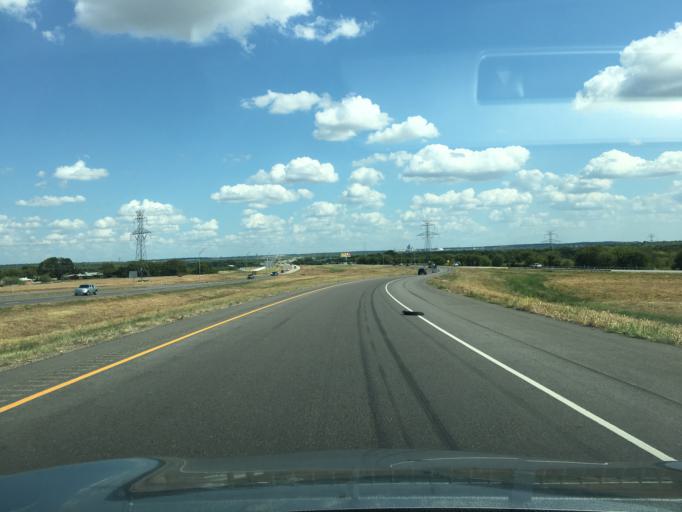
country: US
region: Texas
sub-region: Tarrant County
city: Mansfield
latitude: 32.5210
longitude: -97.0794
